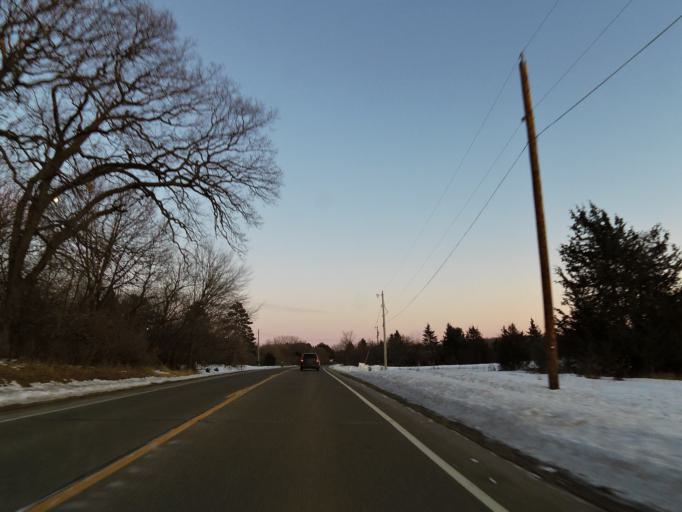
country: US
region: Minnesota
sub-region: Washington County
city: Grant
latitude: 45.0820
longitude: -92.9034
